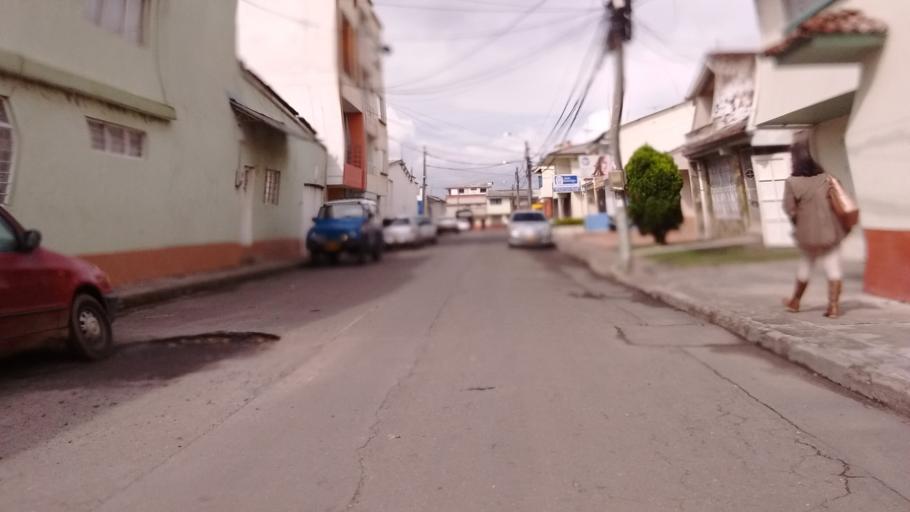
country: CO
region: Cauca
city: Popayan
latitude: 2.4530
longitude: -76.6042
